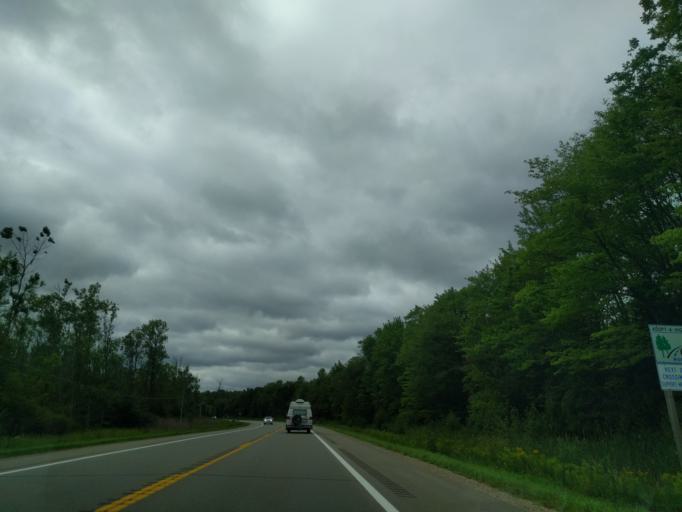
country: US
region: Michigan
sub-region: Menominee County
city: Menominee
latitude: 45.2082
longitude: -87.5326
